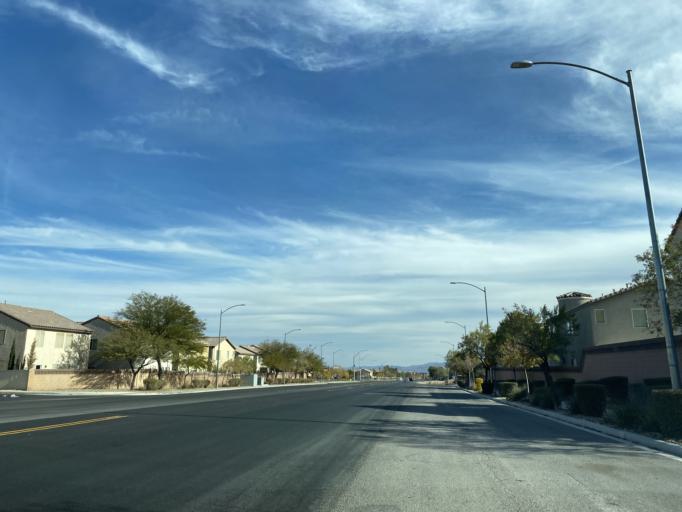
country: US
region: Nevada
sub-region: Clark County
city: Enterprise
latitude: 36.0424
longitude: -115.2105
